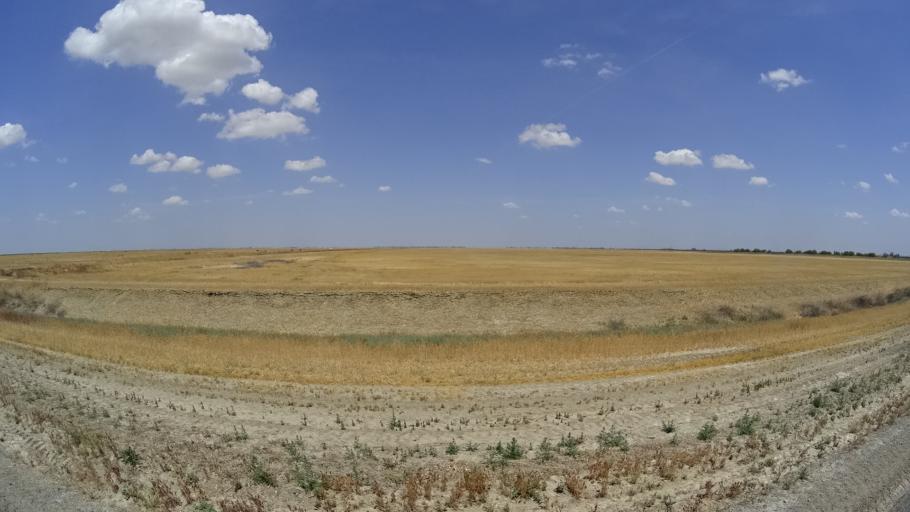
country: US
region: California
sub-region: Kings County
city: Stratford
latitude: 36.1895
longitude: -119.8781
